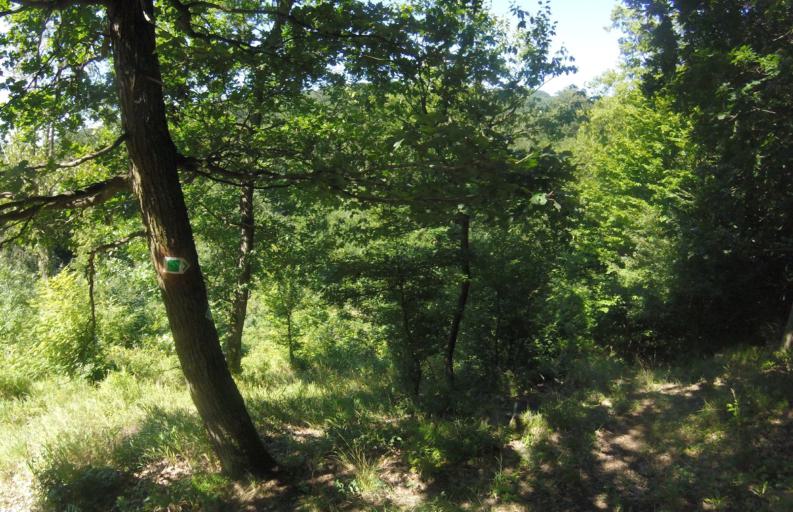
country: HU
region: Pest
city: Szob
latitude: 47.8915
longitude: 18.8734
